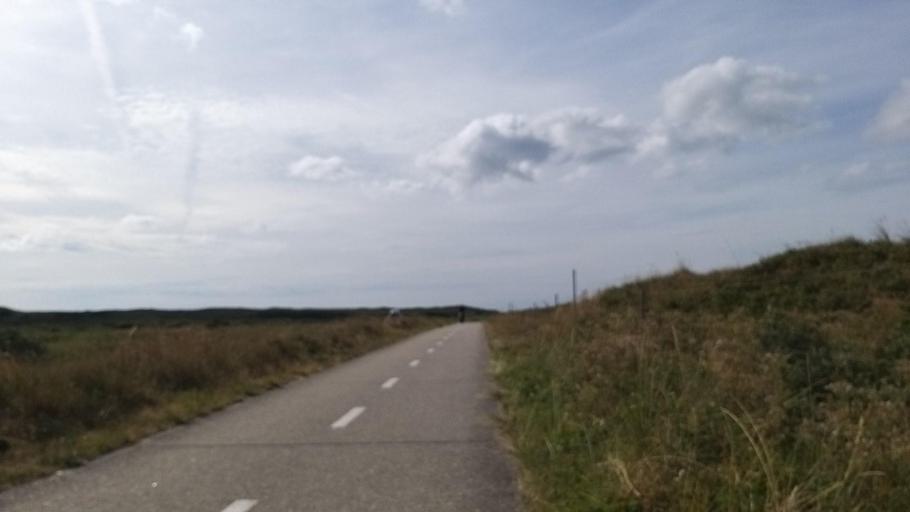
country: NL
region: North Holland
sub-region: Gemeente Texel
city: Den Burg
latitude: 53.1591
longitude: 4.8284
